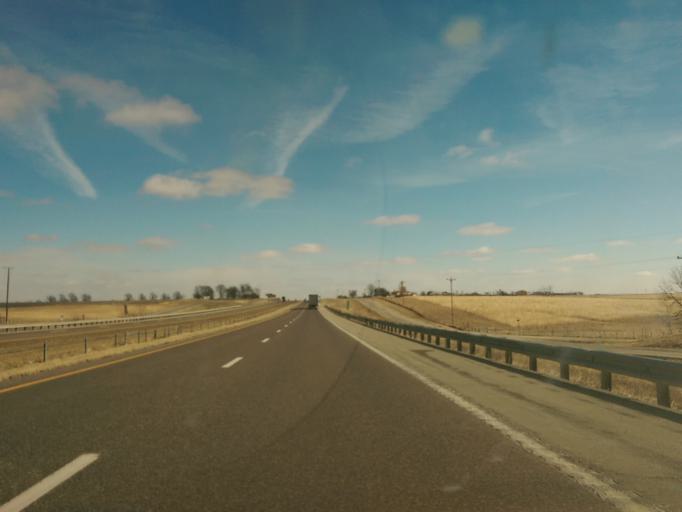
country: US
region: Missouri
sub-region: Callaway County
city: Fulton
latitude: 38.9438
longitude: -91.9102
